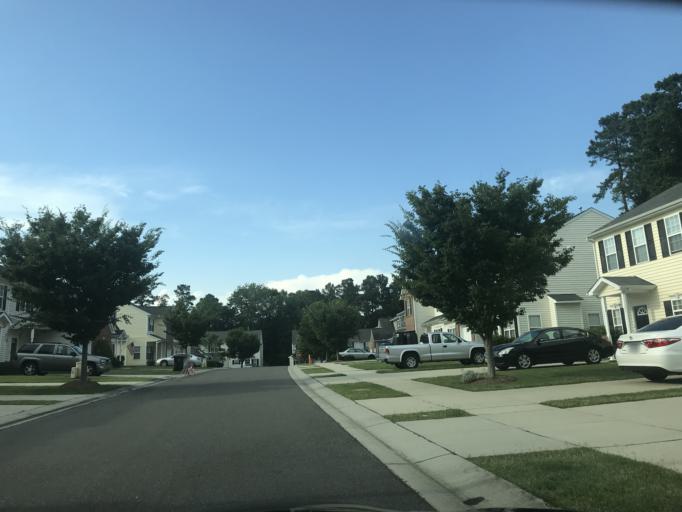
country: US
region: North Carolina
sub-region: Wake County
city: Raleigh
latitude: 35.8280
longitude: -78.5885
